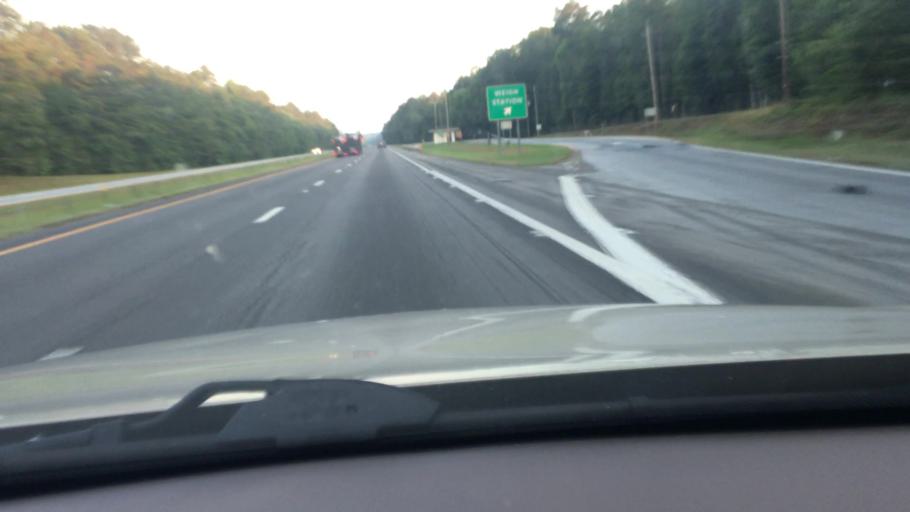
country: US
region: South Carolina
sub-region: Richland County
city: Lake Murray of Richland
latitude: 34.1631
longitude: -81.2820
